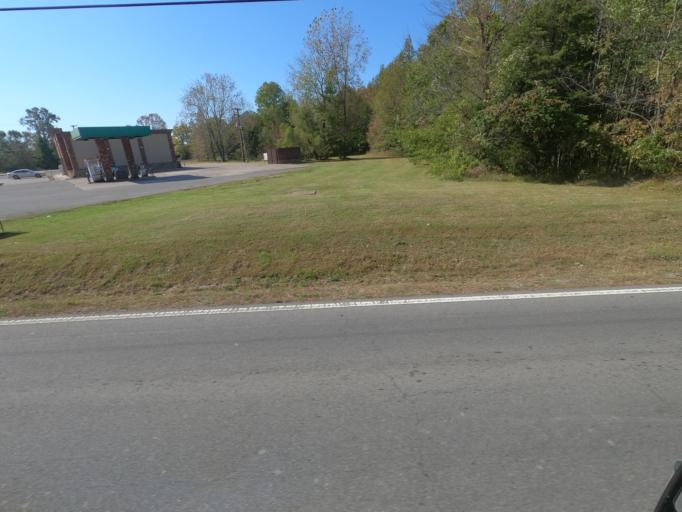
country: US
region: Tennessee
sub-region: Cheatham County
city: Pleasant View
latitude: 36.4439
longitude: -87.1018
